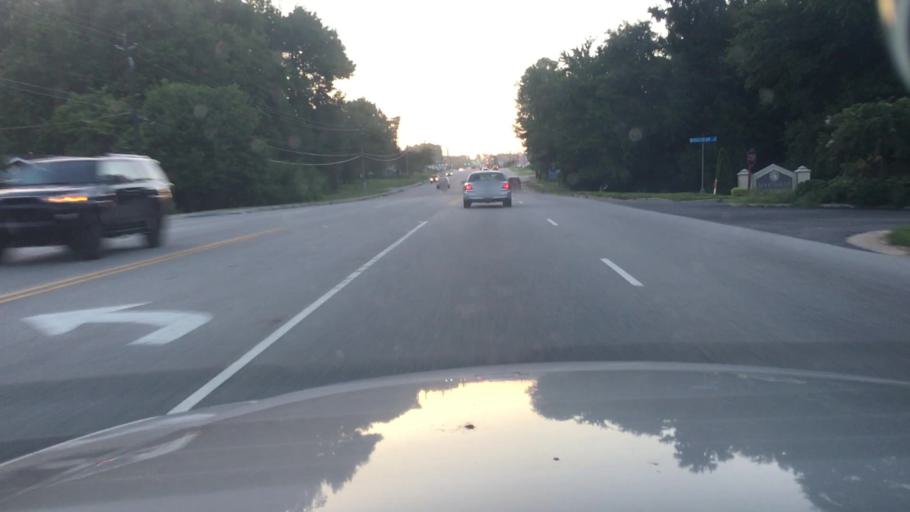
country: US
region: North Carolina
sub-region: Cumberland County
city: Fort Bragg
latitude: 35.0599
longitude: -78.9763
